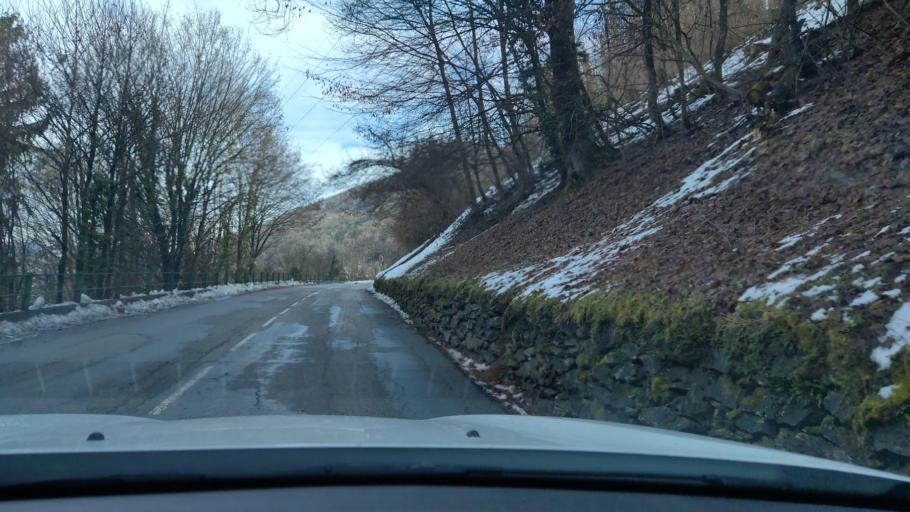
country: FR
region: Rhone-Alpes
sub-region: Departement de la Savoie
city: Albertville
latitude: 45.6974
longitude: 6.4075
